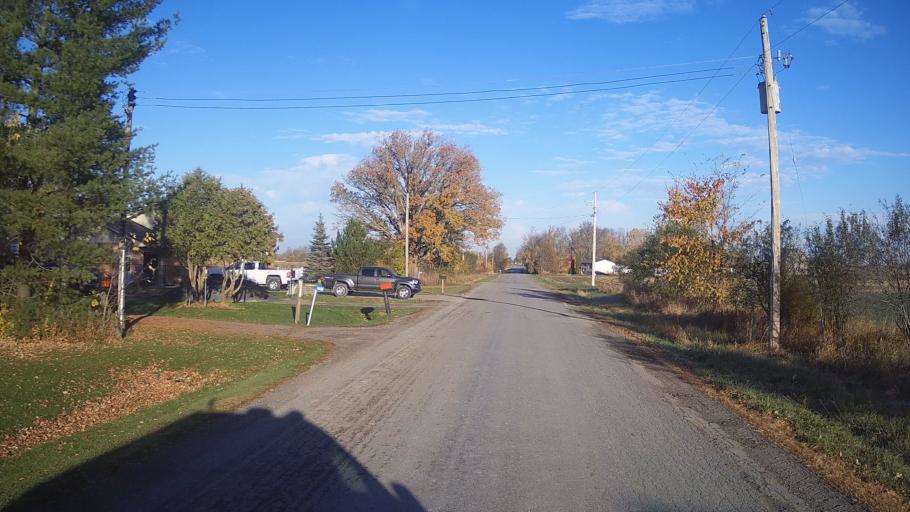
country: CA
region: Ontario
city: Arnprior
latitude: 45.3674
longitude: -76.3206
